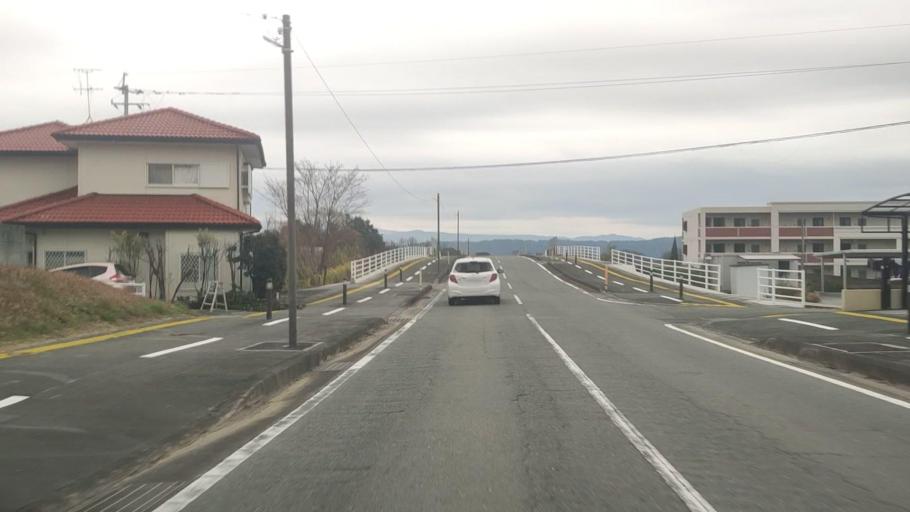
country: JP
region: Kumamoto
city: Ozu
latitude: 32.8769
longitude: 130.8939
